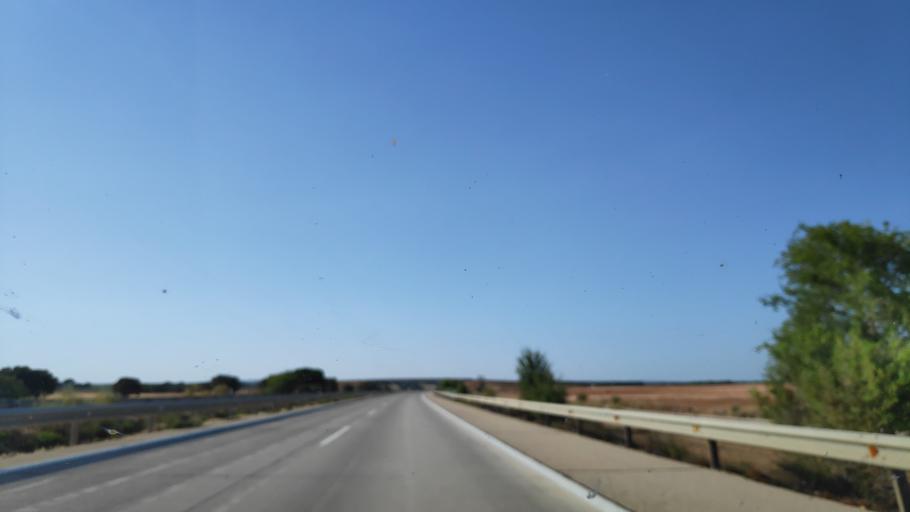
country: ES
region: Castille-La Mancha
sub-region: Provincia de Cuenca
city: Casas de Guijarro
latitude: 39.3114
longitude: -2.2032
